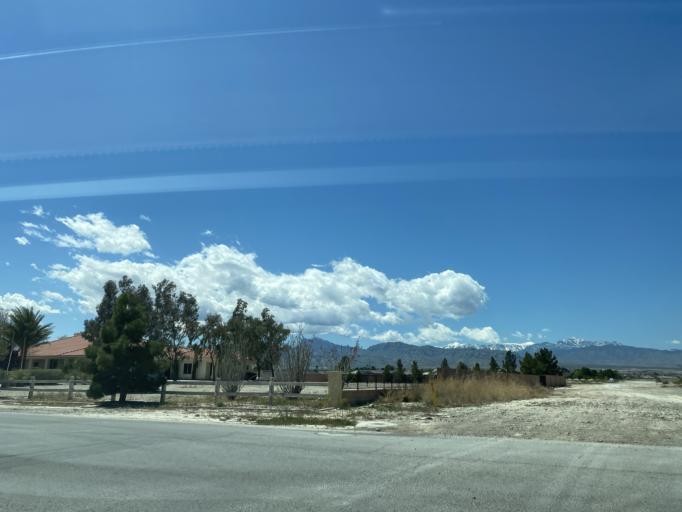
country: US
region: Nevada
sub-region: Clark County
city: North Las Vegas
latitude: 36.3128
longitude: -115.2310
